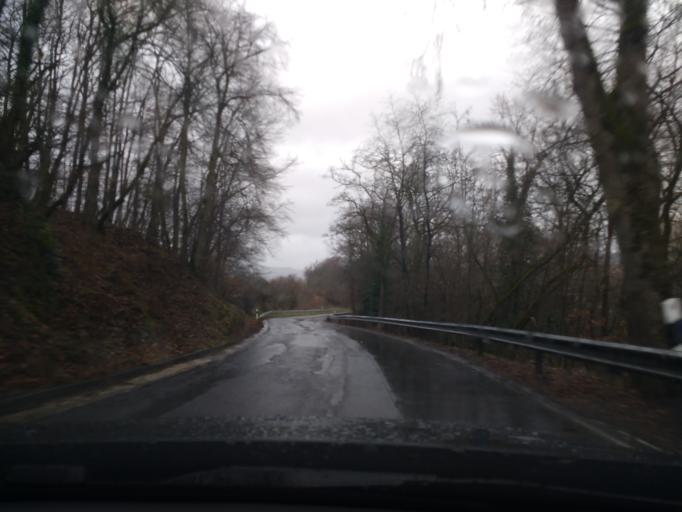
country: DE
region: Rheinland-Pfalz
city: Starkenburg
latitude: 49.9671
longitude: 7.1388
